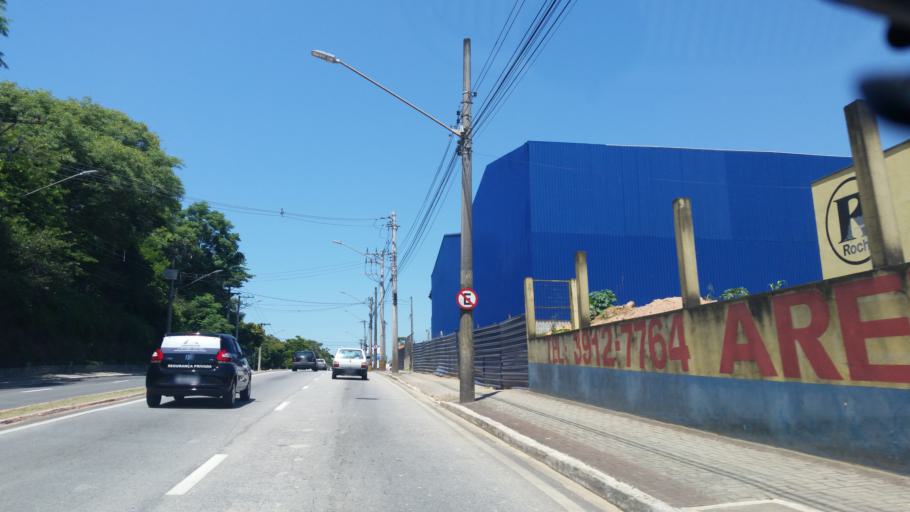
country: BR
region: Sao Paulo
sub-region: Sao Jose Dos Campos
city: Sao Jose dos Campos
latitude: -23.1778
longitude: -45.8325
